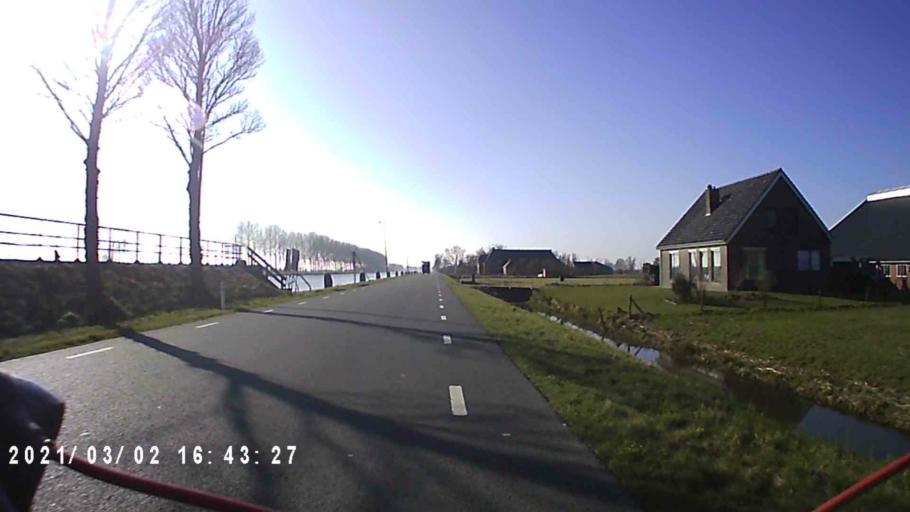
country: NL
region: Groningen
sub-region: Gemeente Zuidhorn
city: Grijpskerk
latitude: 53.2486
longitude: 6.3054
